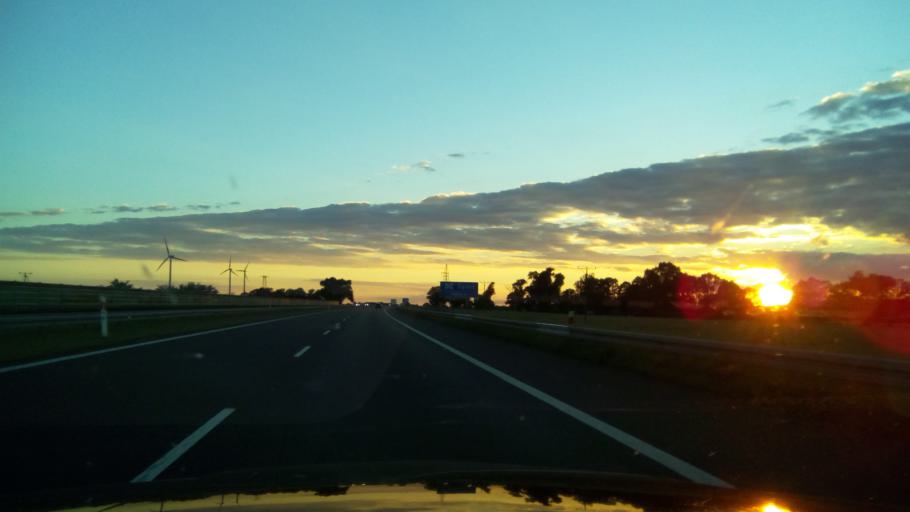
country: PL
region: Lodz Voivodeship
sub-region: Powiat zgierski
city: Zgierz
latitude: 51.8982
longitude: 19.4825
